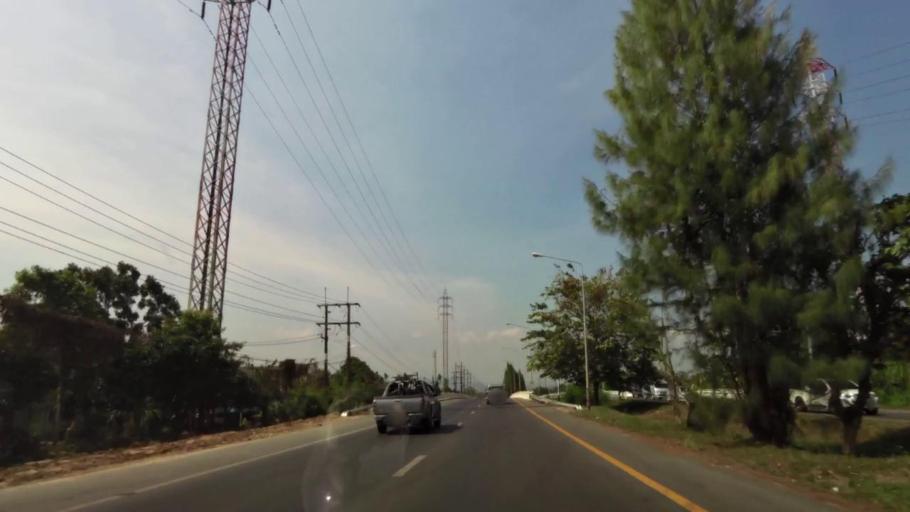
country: TH
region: Chanthaburi
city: Chanthaburi
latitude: 12.6360
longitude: 102.1384
